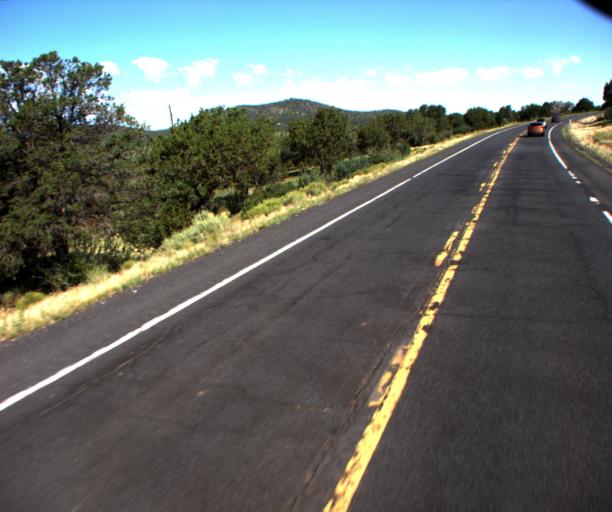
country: US
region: Arizona
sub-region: Coconino County
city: Williams
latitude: 35.3425
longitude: -112.1650
